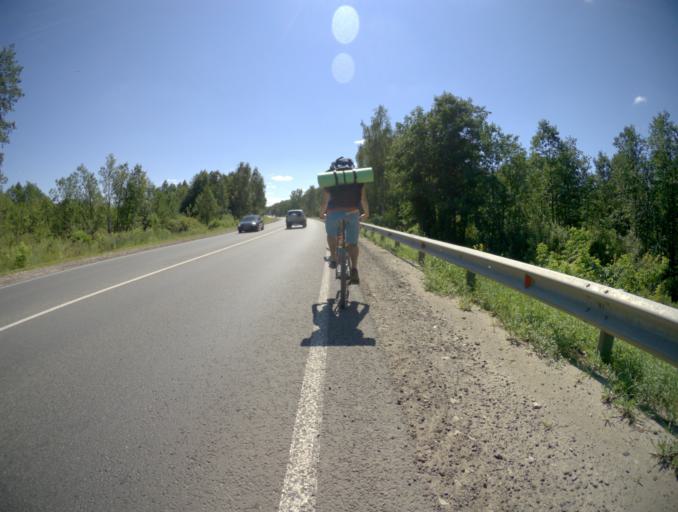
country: RU
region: Nizjnij Novgorod
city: Neklyudovo
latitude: 56.4287
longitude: 43.9899
